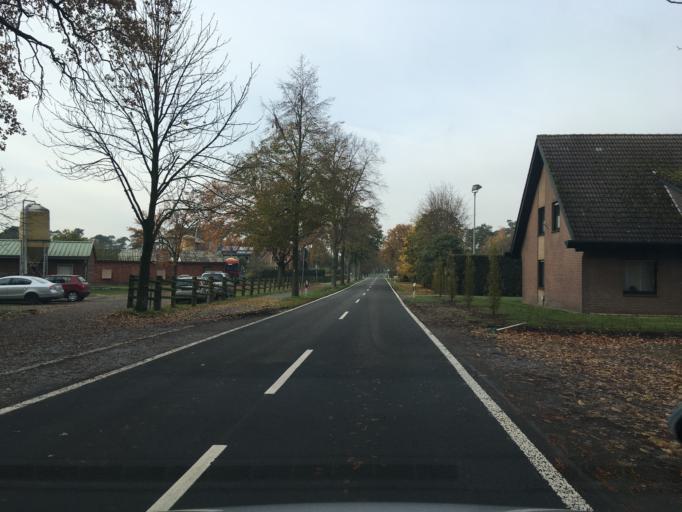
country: DE
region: North Rhine-Westphalia
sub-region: Regierungsbezirk Munster
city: Velen
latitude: 51.9175
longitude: 6.9623
